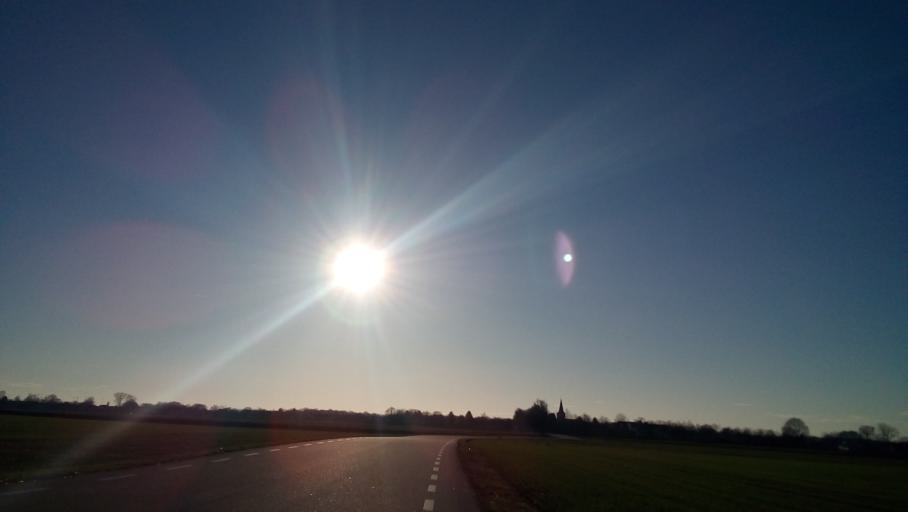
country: DE
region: Baden-Wuerttemberg
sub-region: Karlsruhe Region
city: Zell
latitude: 48.6643
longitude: 8.0311
